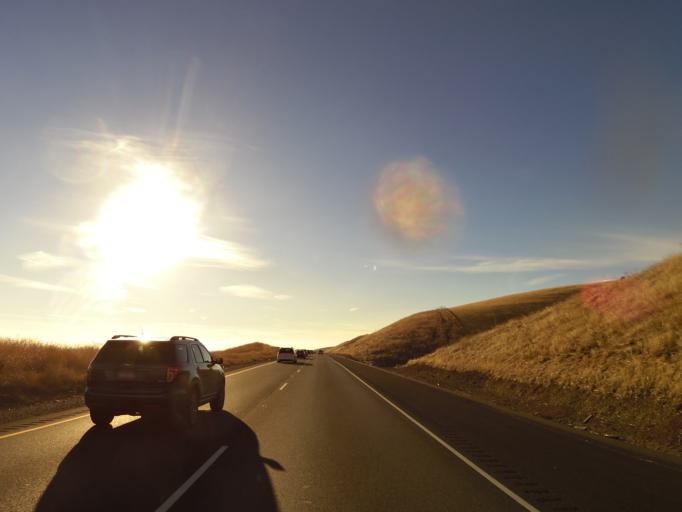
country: US
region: California
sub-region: Stanislaus County
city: Patterson
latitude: 37.4462
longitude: -121.1678
